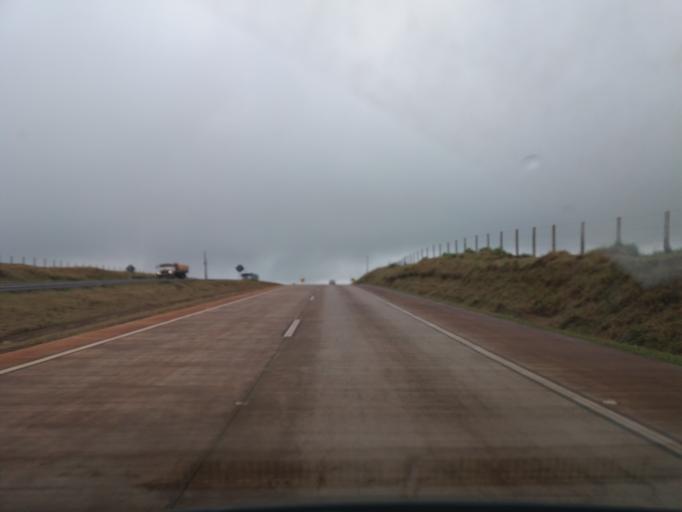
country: BR
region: Parana
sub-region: Cascavel
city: Cascavel
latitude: -25.1103
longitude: -53.5886
